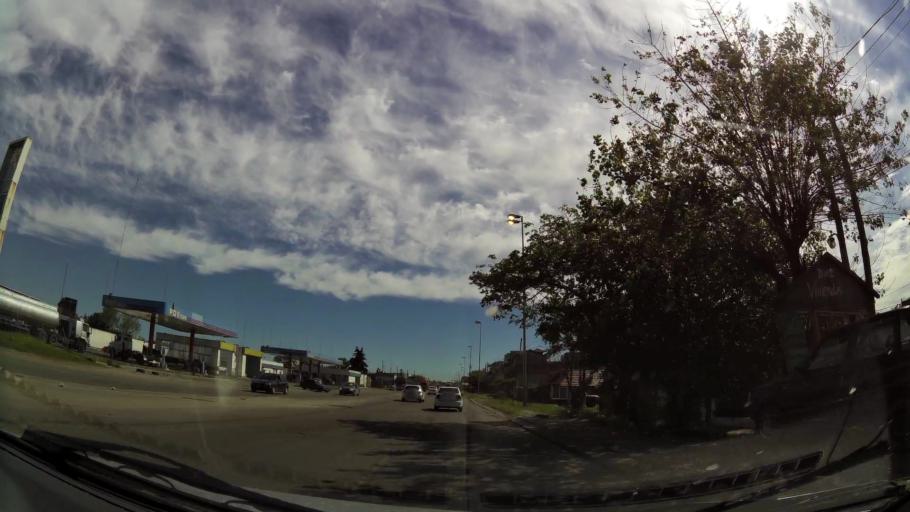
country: AR
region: Buenos Aires
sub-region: Partido de Almirante Brown
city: Adrogue
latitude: -34.7883
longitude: -58.3068
